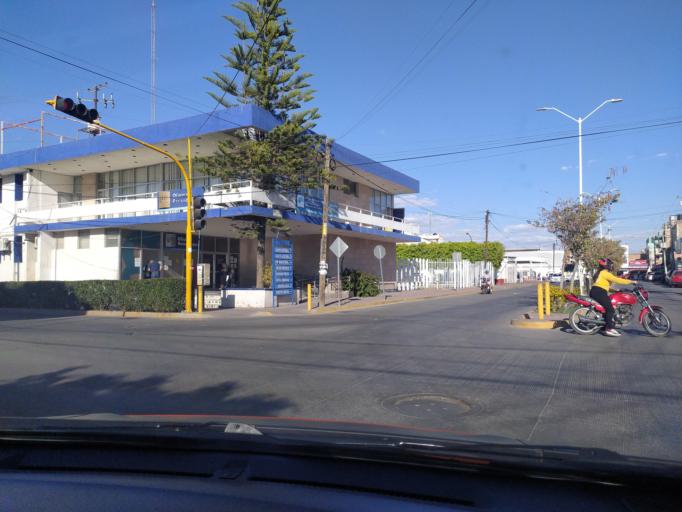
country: LA
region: Oudomxai
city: Muang La
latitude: 21.0141
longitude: 101.8590
